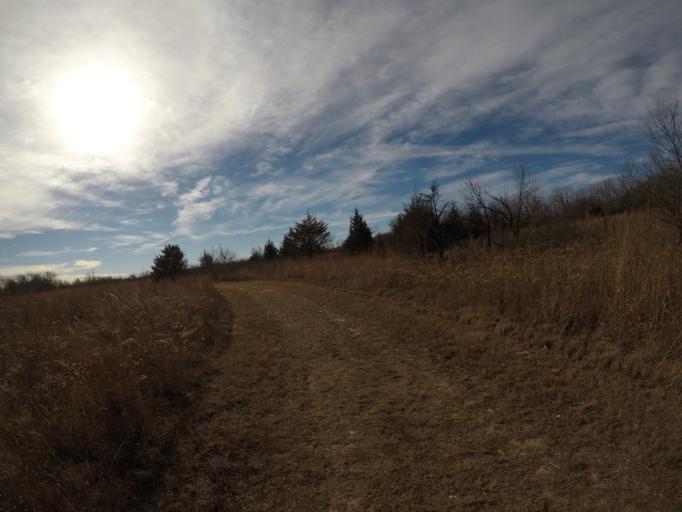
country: US
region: Kansas
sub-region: Reno County
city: Buhler
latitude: 38.1222
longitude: -97.8574
